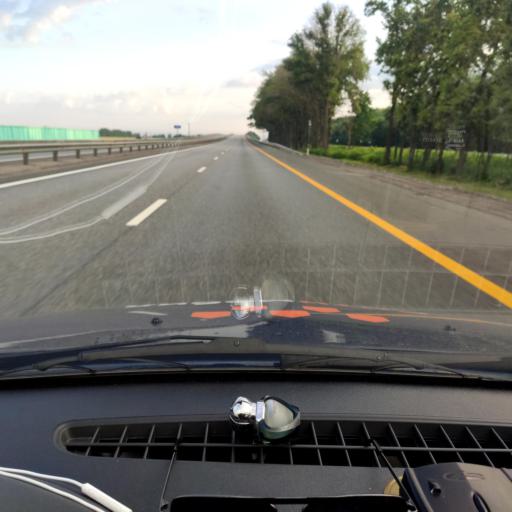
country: RU
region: Lipetsk
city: Zadonsk
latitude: 52.4539
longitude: 38.7786
